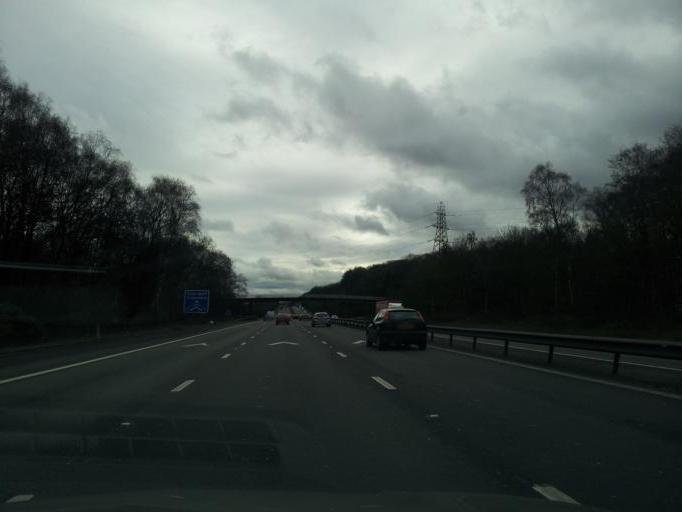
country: GB
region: England
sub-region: Staffordshire
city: Newcastle under Lyme
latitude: 52.9533
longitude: -2.2186
